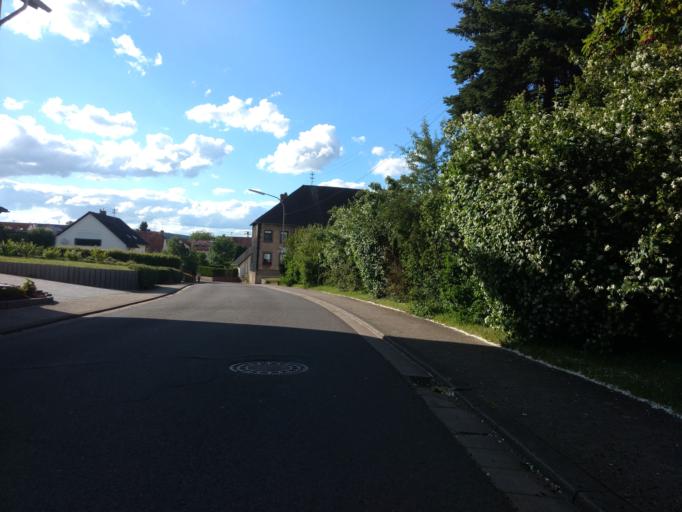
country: DE
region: Saarland
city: Merzig
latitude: 49.4470
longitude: 6.6128
